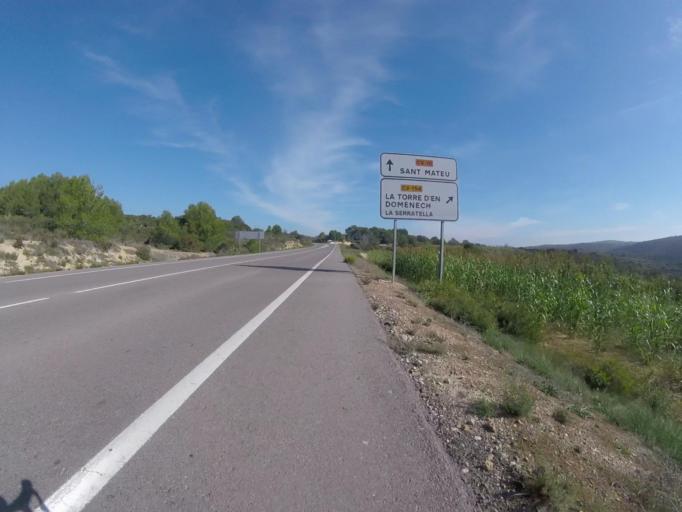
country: ES
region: Valencia
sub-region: Provincia de Castello
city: Benlloch
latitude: 40.2564
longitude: 0.0769
